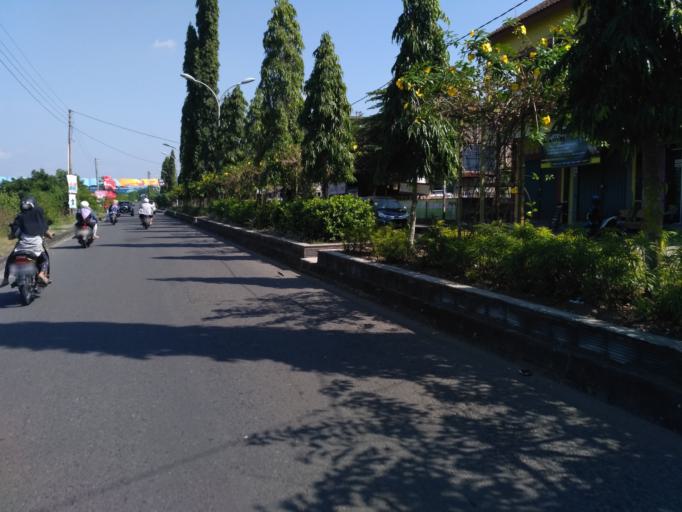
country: ID
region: Daerah Istimewa Yogyakarta
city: Depok
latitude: -7.7508
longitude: 110.4249
